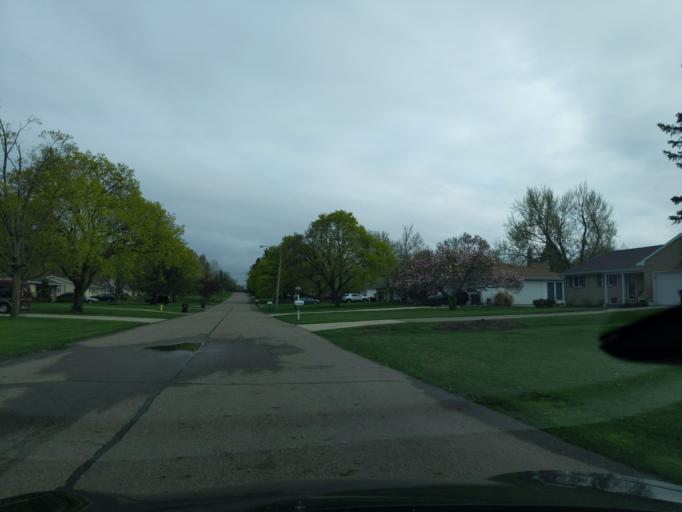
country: US
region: Michigan
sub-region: Eaton County
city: Waverly
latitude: 42.7322
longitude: -84.6103
